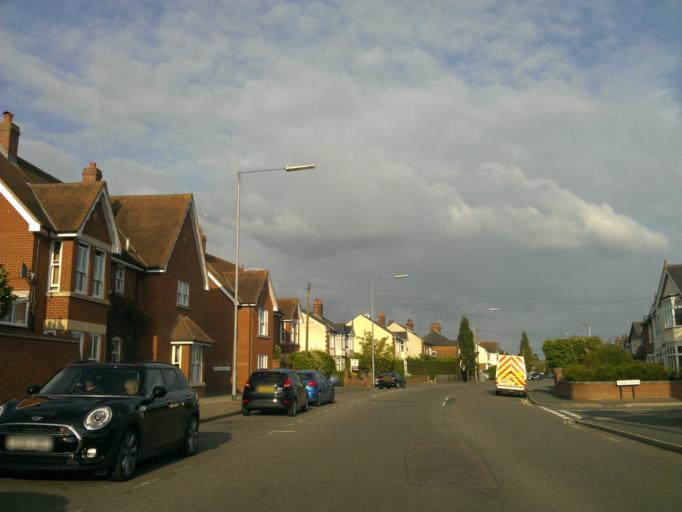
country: GB
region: England
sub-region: Essex
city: Colchester
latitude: 51.8796
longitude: 0.8801
